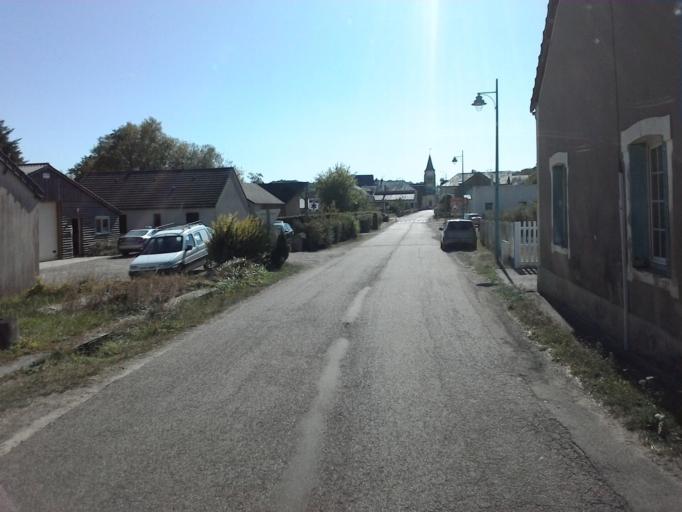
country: FR
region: Bourgogne
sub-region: Departement de la Nievre
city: Lormes
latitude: 47.2638
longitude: 3.9384
